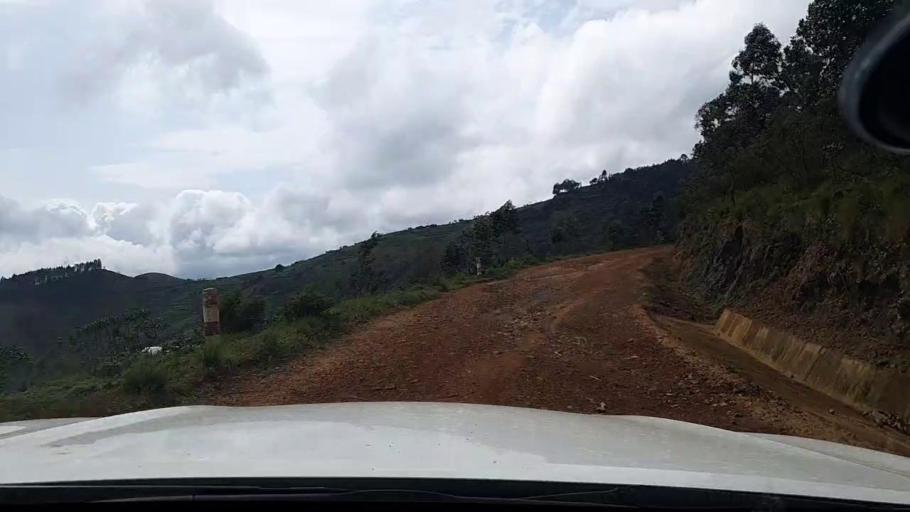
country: RW
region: Western Province
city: Kibuye
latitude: -2.1316
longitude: 29.3780
